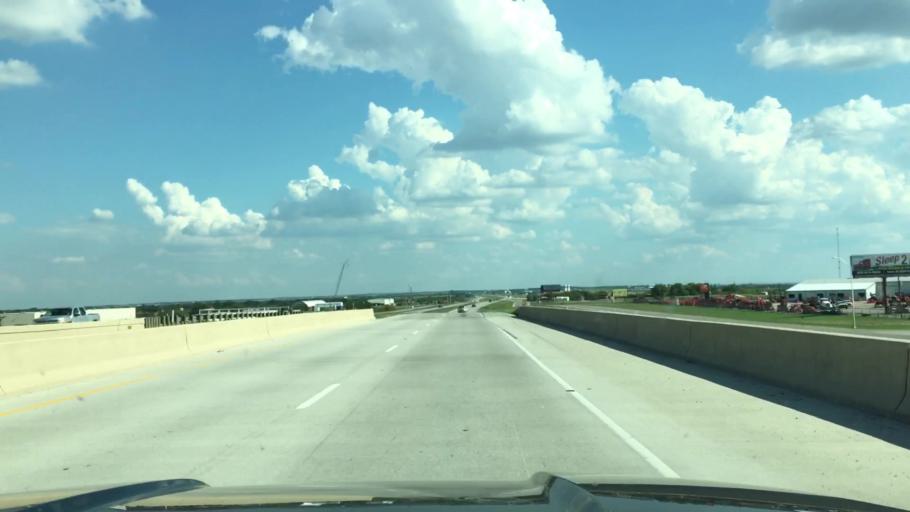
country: US
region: Texas
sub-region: Wise County
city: Decatur
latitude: 33.2037
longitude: -97.5670
